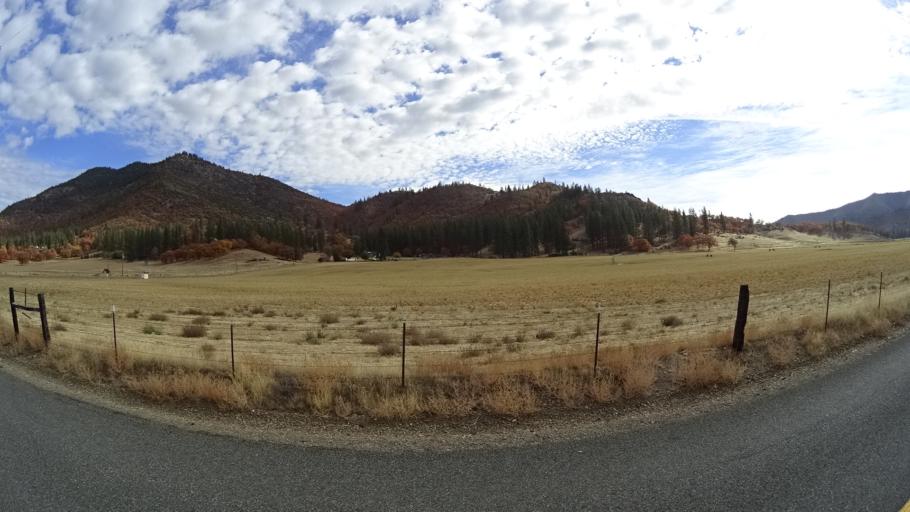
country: US
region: California
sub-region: Siskiyou County
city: Yreka
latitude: 41.6387
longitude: -122.8299
